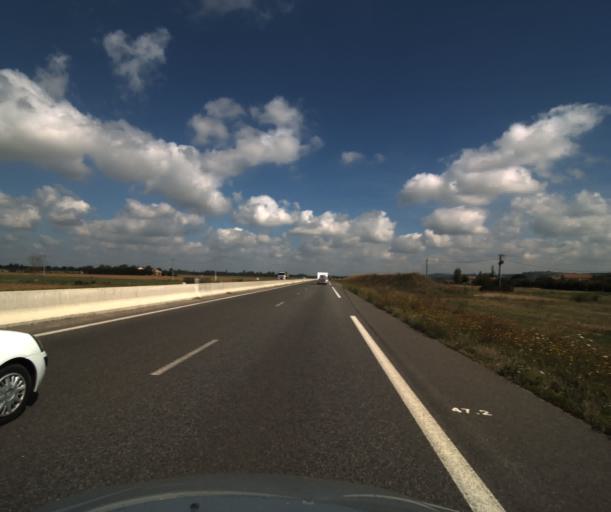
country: FR
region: Midi-Pyrenees
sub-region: Departement de la Haute-Garonne
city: Vernet
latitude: 43.4336
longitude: 1.4167
